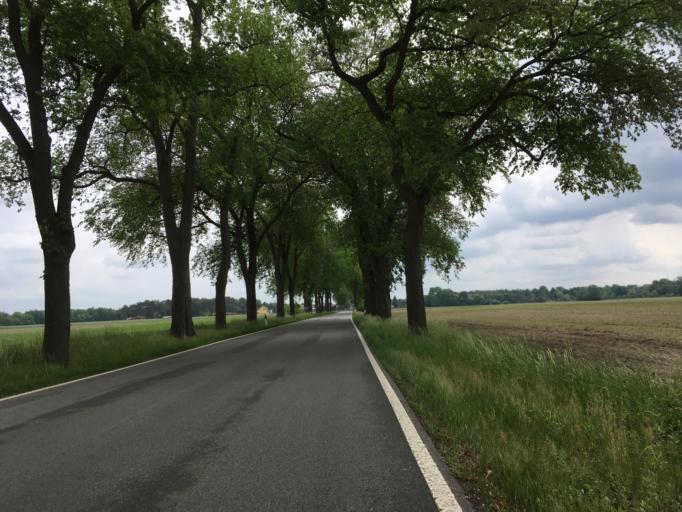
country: DE
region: Brandenburg
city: Marienwerder
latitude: 52.8407
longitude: 13.5815
